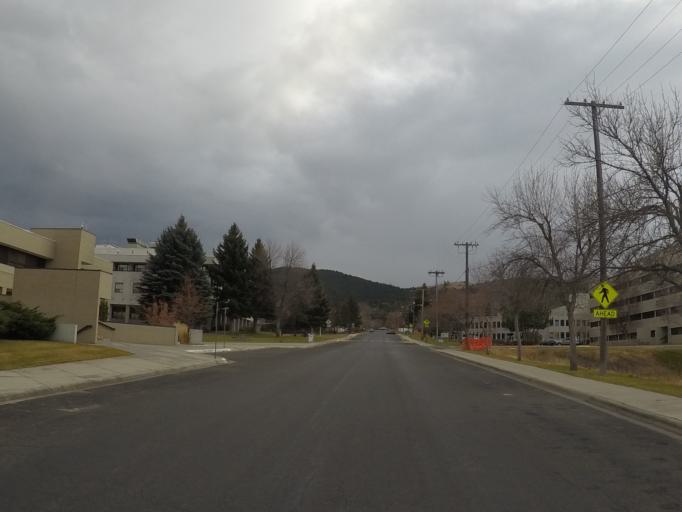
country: US
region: Montana
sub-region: Lewis and Clark County
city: Helena
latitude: 46.5865
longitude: -112.0147
